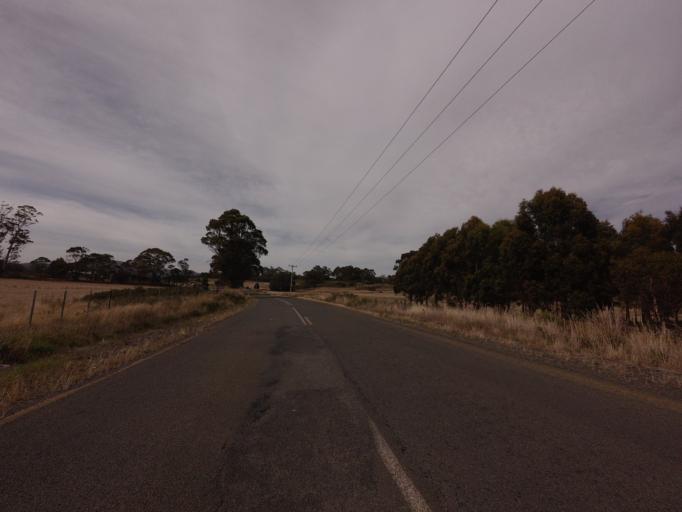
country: AU
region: Tasmania
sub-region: Sorell
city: Sorell
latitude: -42.4128
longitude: 147.4570
